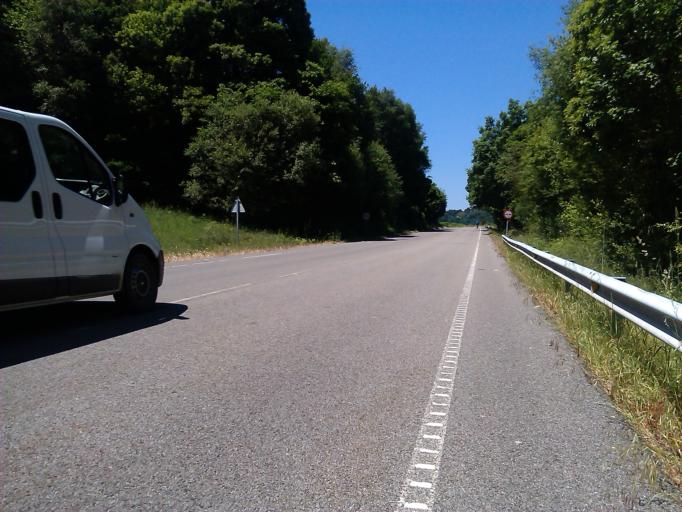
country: ES
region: Galicia
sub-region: Provincia de Lugo
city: Samos
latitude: 42.7381
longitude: -7.3011
